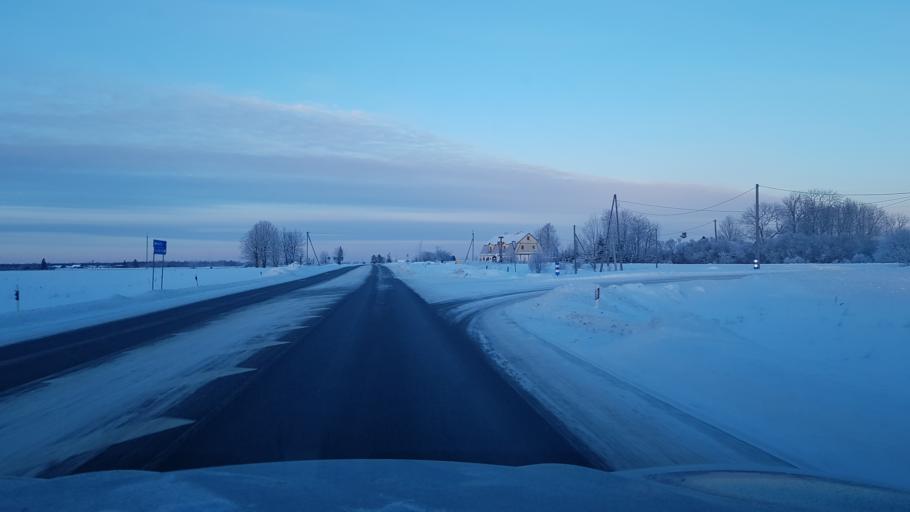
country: EE
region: Ida-Virumaa
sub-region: Narva-Joesuu linn
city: Narva-Joesuu
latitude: 59.4008
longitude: 28.0656
